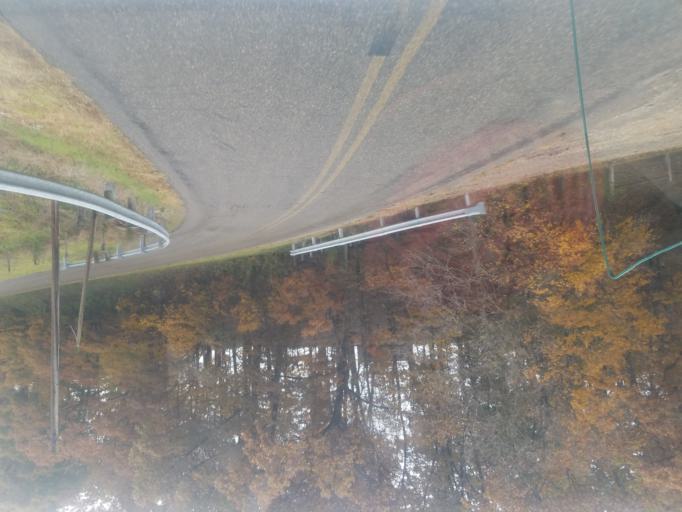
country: US
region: Ohio
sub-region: Washington County
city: Beverly
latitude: 39.5543
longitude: -81.6806
